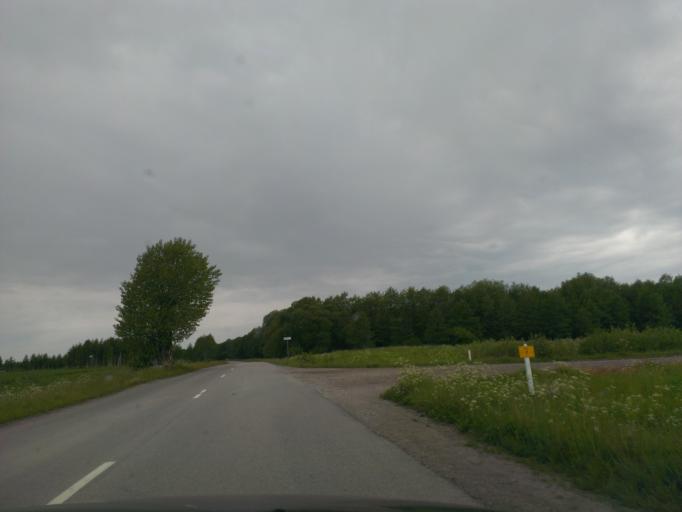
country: LT
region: Klaipedos apskritis
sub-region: Klaipeda
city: Palanga
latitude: 55.8235
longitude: 21.0966
